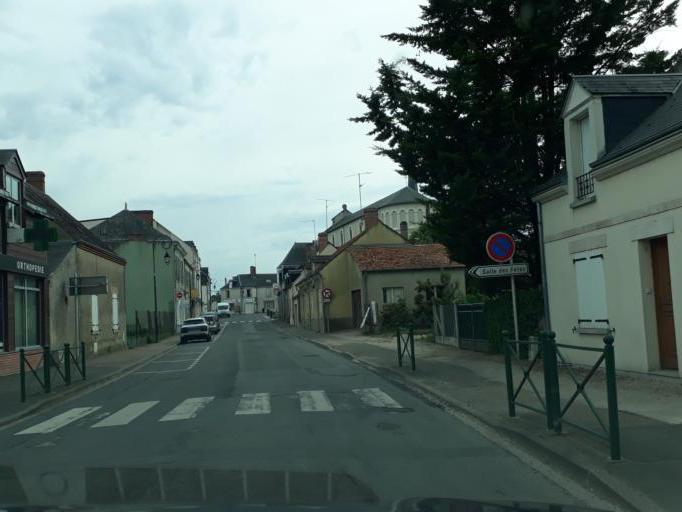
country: FR
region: Centre
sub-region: Departement du Loiret
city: Sandillon
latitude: 47.8467
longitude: 2.0338
